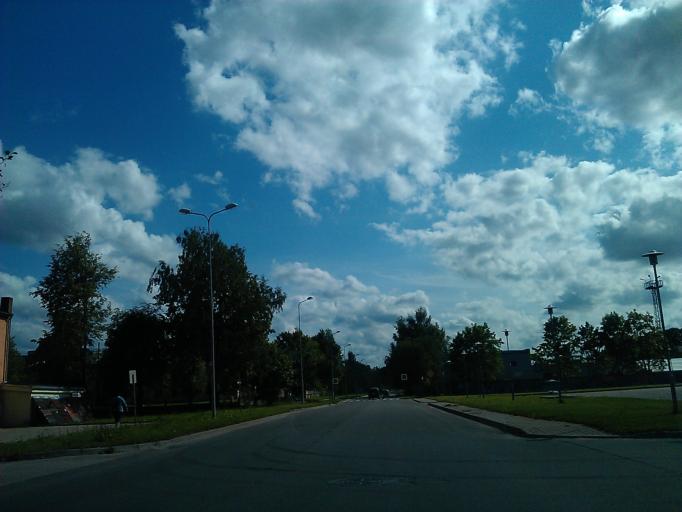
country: LV
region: Cesu Rajons
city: Cesis
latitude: 57.3132
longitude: 25.2869
